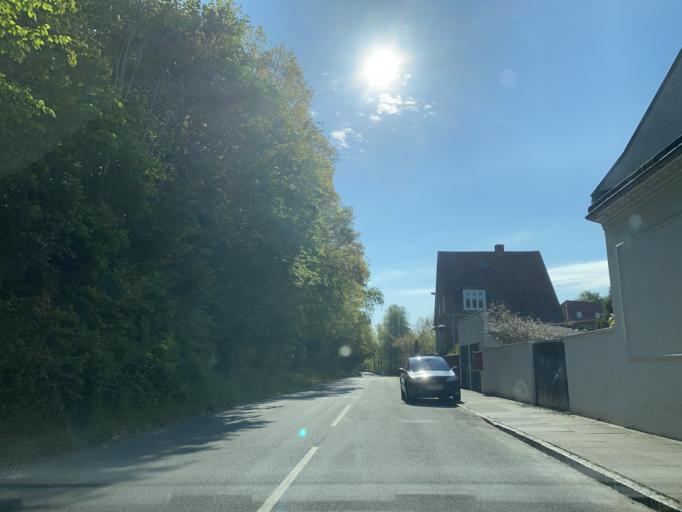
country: DK
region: Central Jutland
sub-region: Silkeborg Kommune
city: Silkeborg
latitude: 56.1634
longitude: 9.5358
